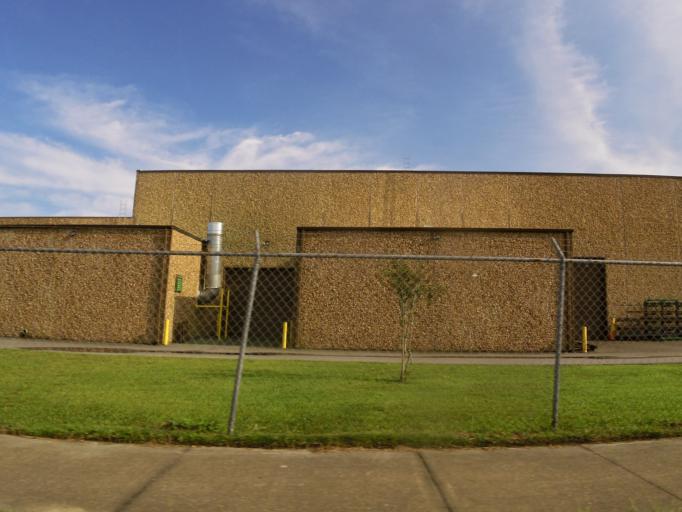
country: US
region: Florida
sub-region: Saint Johns County
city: Fruit Cove
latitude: 30.1942
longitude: -81.5736
